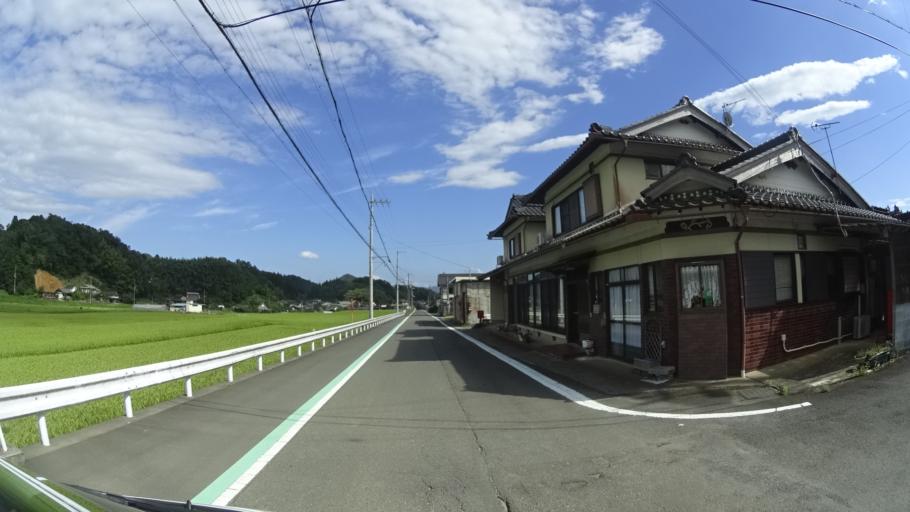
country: JP
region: Kyoto
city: Fukuchiyama
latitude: 35.3305
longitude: 135.1738
